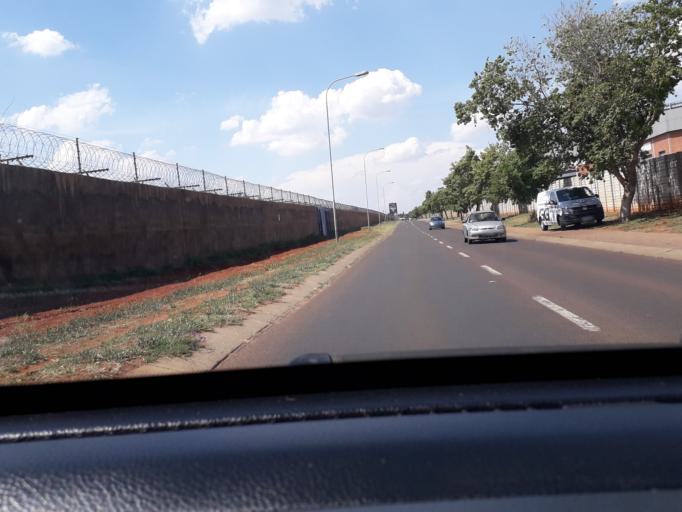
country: ZA
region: Gauteng
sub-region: City of Tshwane Metropolitan Municipality
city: Centurion
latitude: -25.8433
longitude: 28.2292
